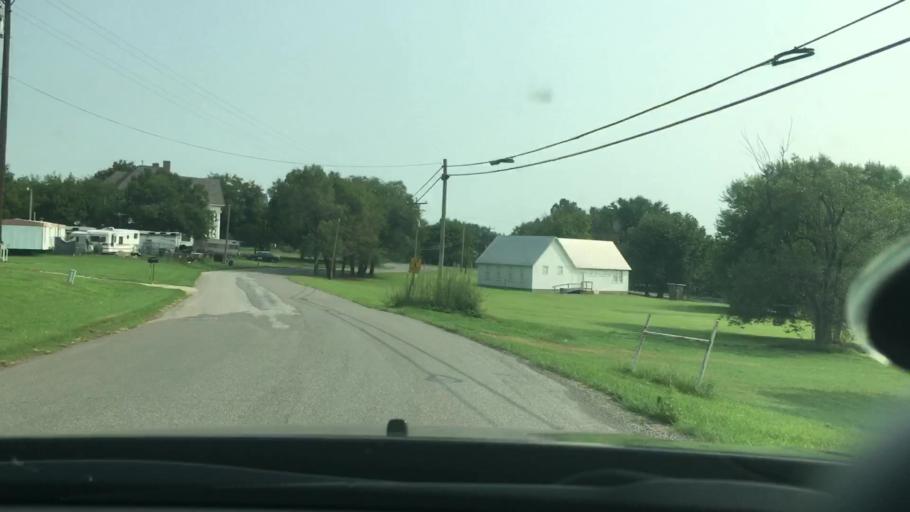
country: US
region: Oklahoma
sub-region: Garvin County
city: Lindsay
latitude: 34.8103
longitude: -97.6080
